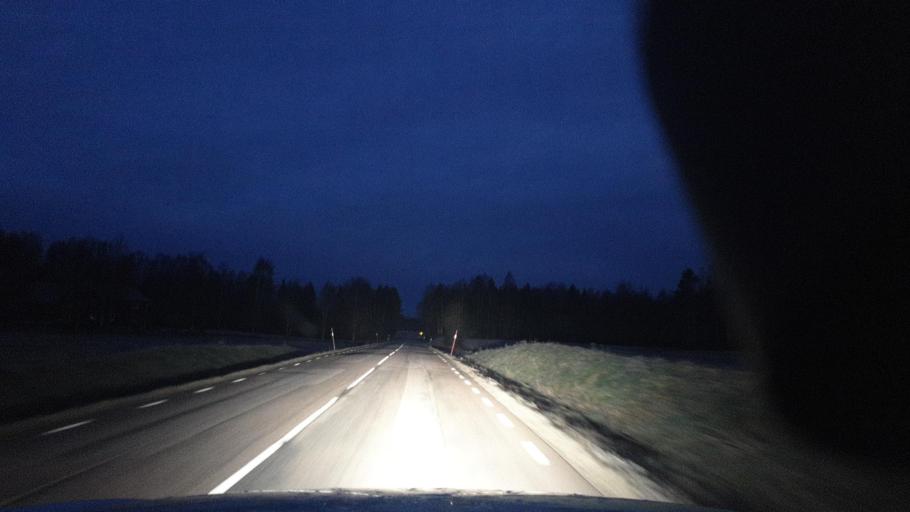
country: SE
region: Vaermland
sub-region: Eda Kommun
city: Charlottenberg
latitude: 59.9075
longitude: 12.2946
